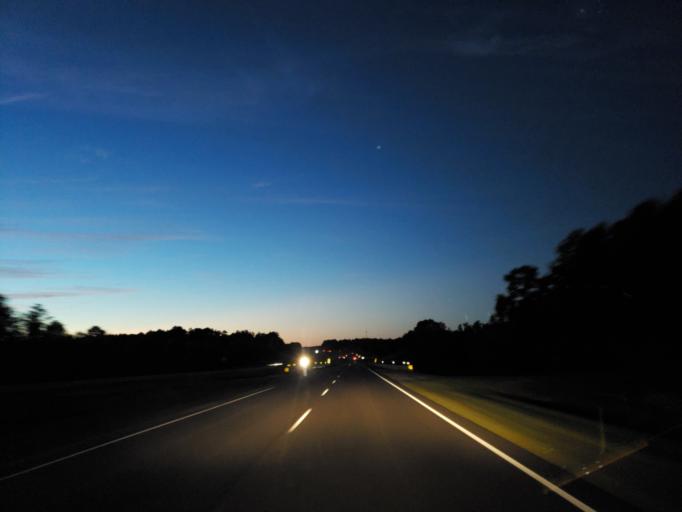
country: US
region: Mississippi
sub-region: Clarke County
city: Quitman
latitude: 32.0959
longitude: -88.7028
